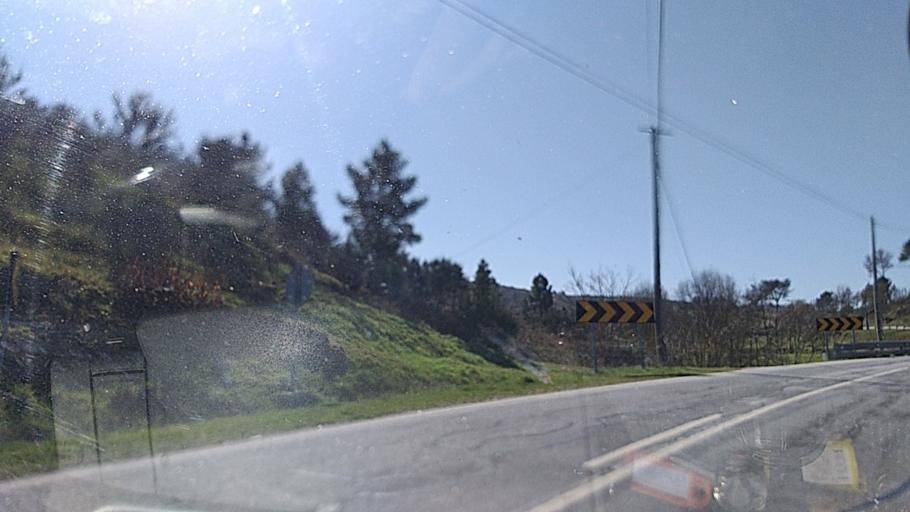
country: PT
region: Guarda
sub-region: Celorico da Beira
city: Celorico da Beira
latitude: 40.6010
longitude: -7.4250
